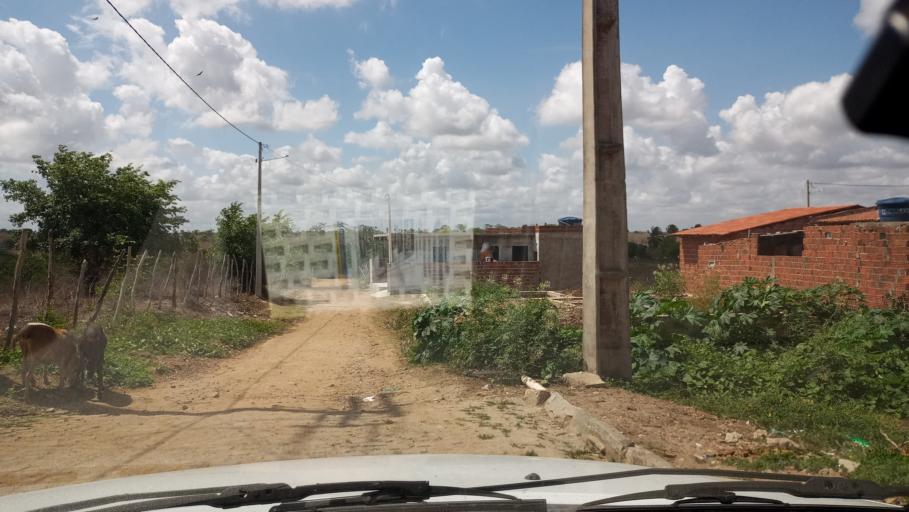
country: BR
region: Rio Grande do Norte
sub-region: Santo Antonio
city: Santo Antonio
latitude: -6.3462
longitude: -35.3700
